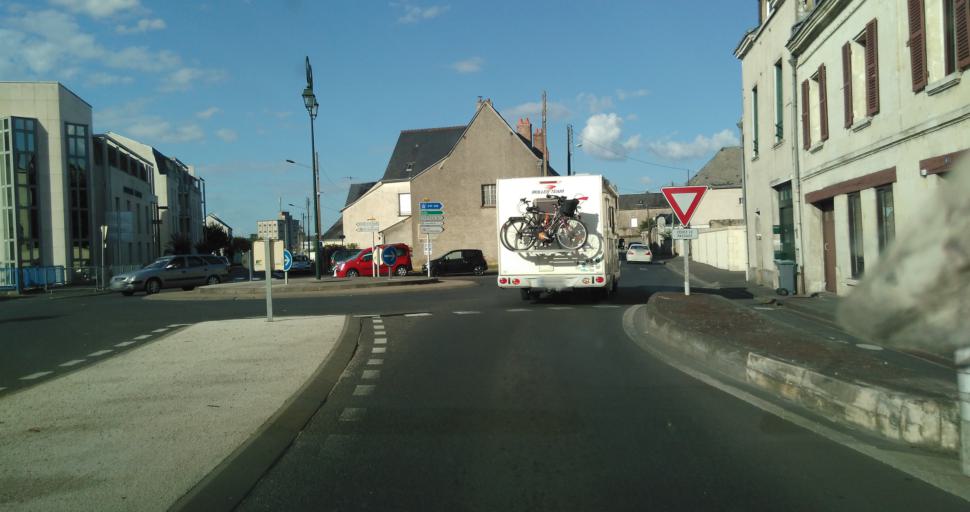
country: FR
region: Centre
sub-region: Departement d'Indre-et-Loire
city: Amboise
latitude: 47.4182
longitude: 0.9823
